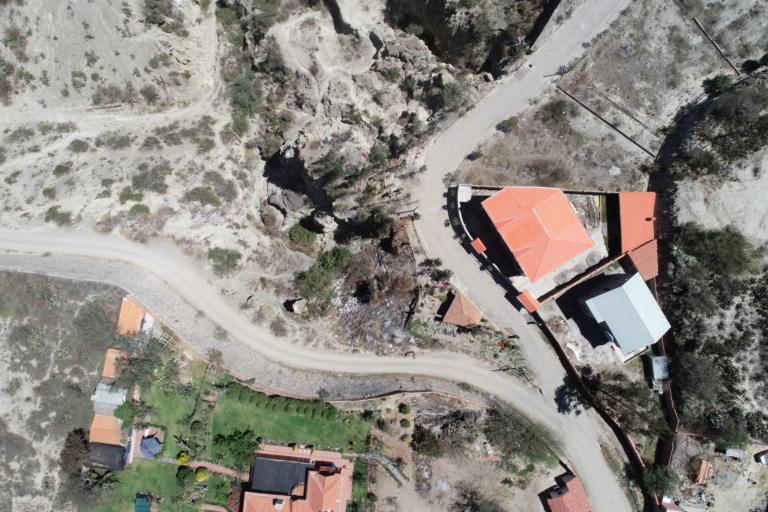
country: BO
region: La Paz
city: La Paz
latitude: -16.6304
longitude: -68.0556
